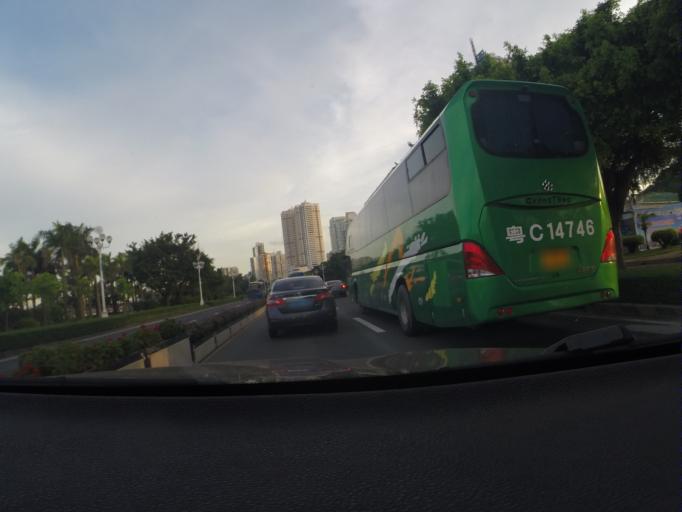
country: CN
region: Guangdong
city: Zhuhai
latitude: 22.2980
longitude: 113.5732
